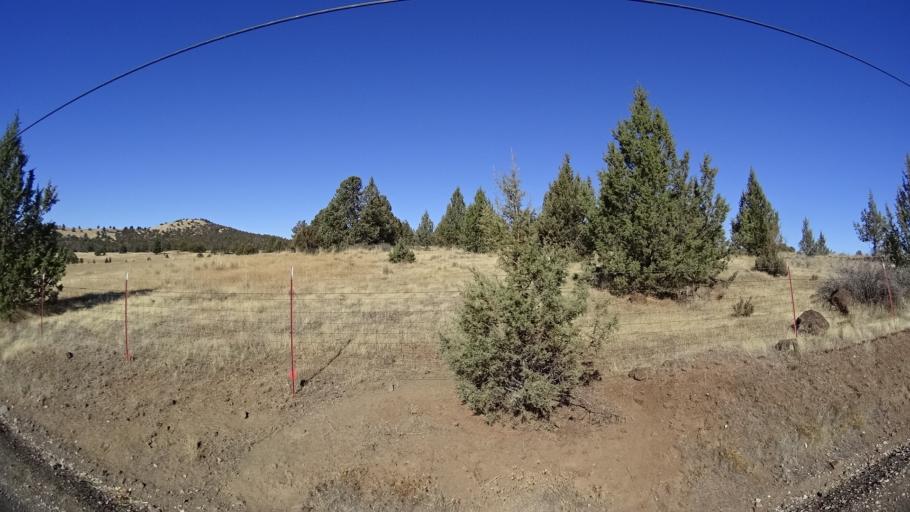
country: US
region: California
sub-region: Siskiyou County
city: Montague
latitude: 41.9510
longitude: -122.3347
